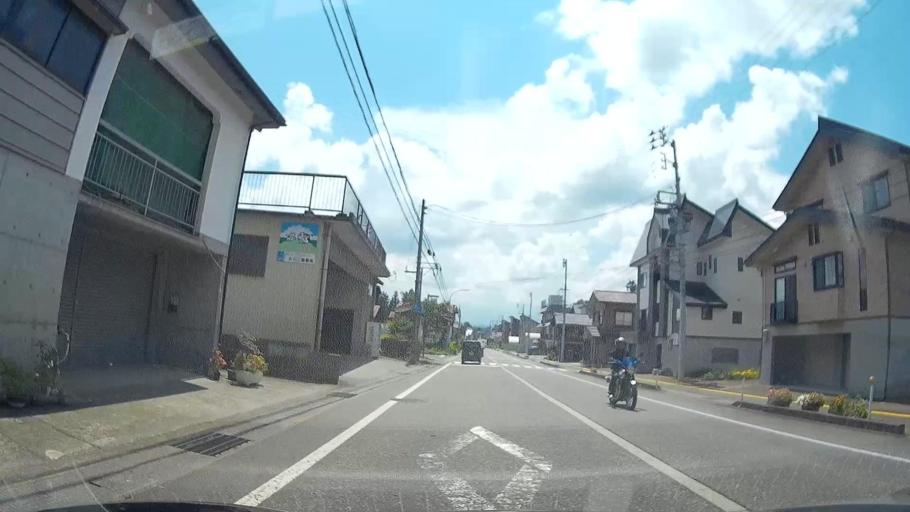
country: JP
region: Niigata
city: Tokamachi
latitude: 37.0801
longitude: 138.7203
